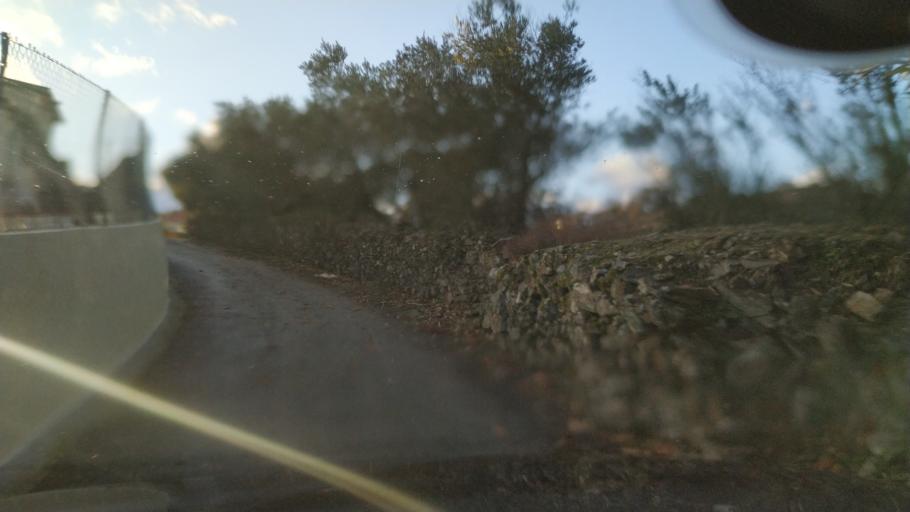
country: PT
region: Vila Real
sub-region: Vila Real
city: Vila Real
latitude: 41.2558
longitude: -7.7573
